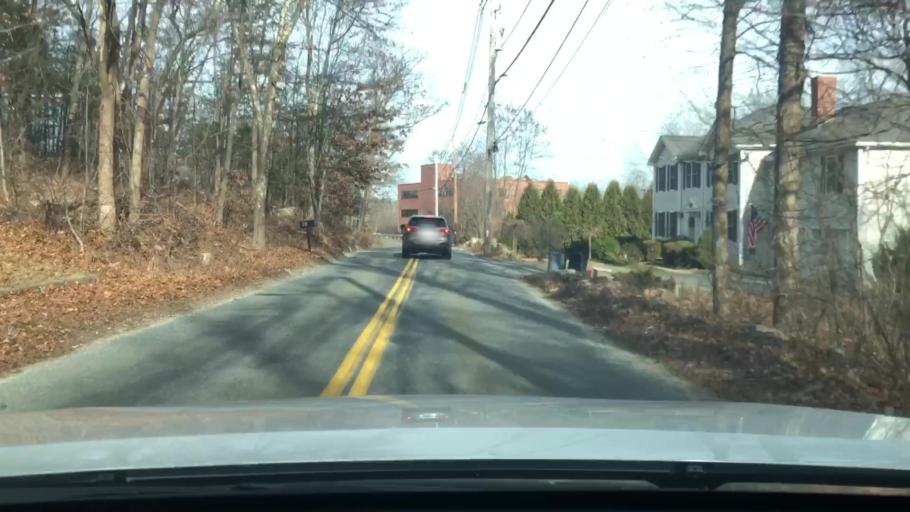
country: US
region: Massachusetts
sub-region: Worcester County
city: Milford
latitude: 42.1389
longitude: -71.4882
